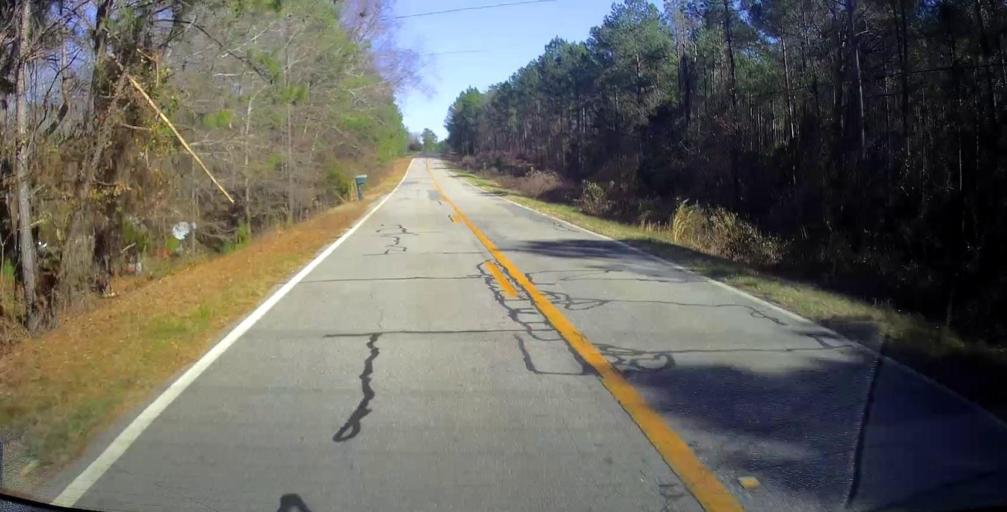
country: US
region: Georgia
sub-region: Peach County
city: Byron
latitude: 32.6112
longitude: -83.8266
